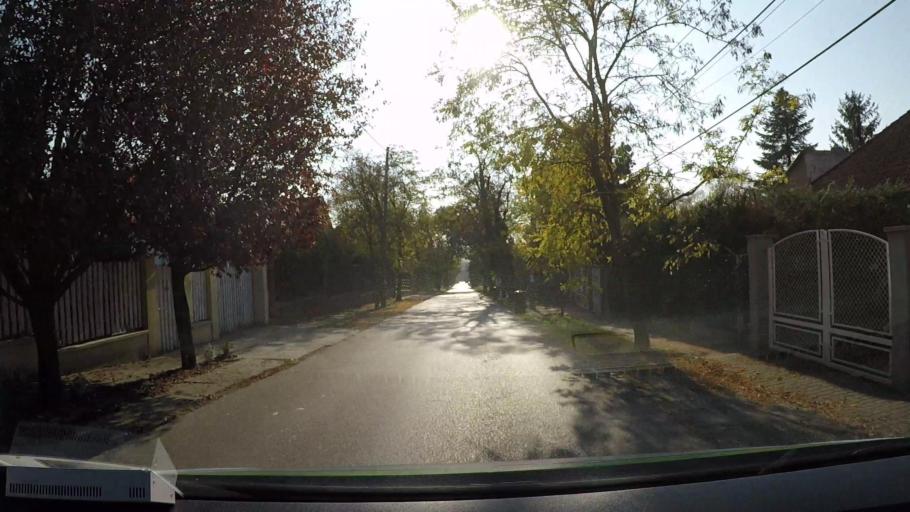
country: HU
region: Budapest
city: Budapest XXII. keruelet
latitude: 47.4154
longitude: 19.0287
